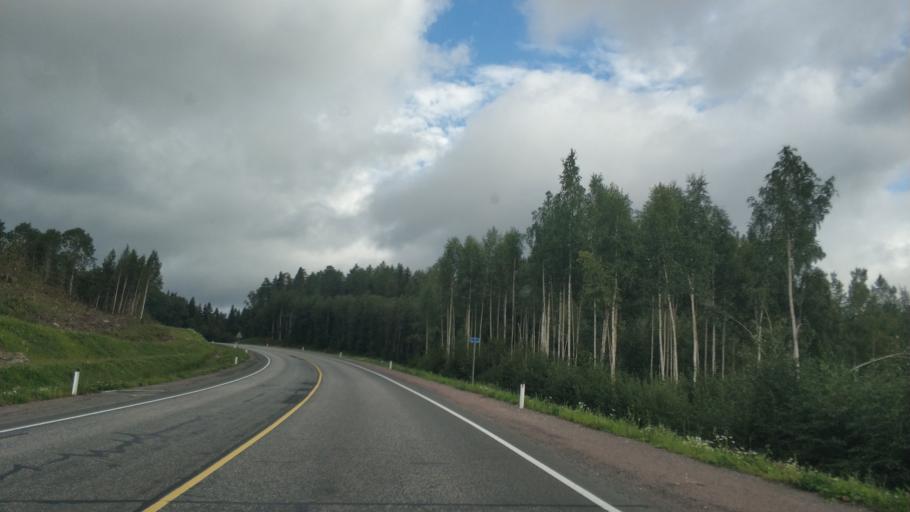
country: RU
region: Republic of Karelia
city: Khelyulya
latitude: 61.8250
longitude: 30.6359
